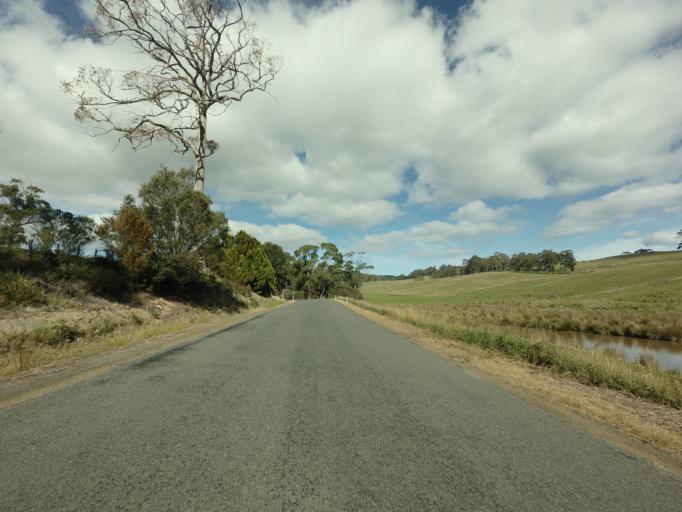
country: AU
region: Tasmania
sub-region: Clarence
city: Sandford
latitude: -43.0346
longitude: 147.7318
